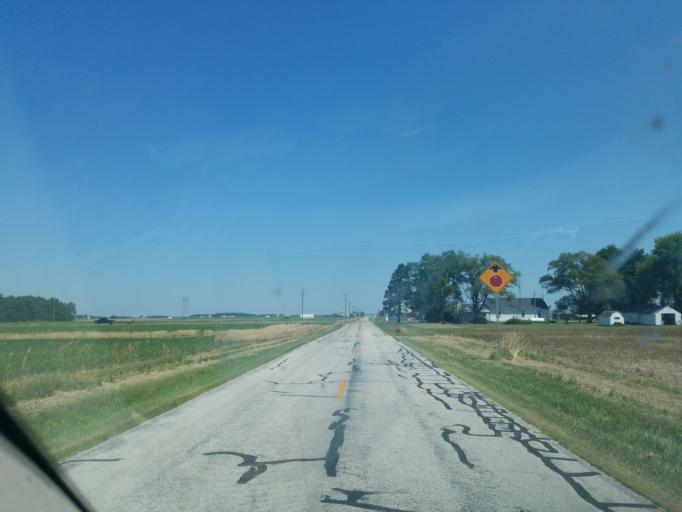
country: US
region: Ohio
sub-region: Mercer County
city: Rockford
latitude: 40.6097
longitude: -84.7085
